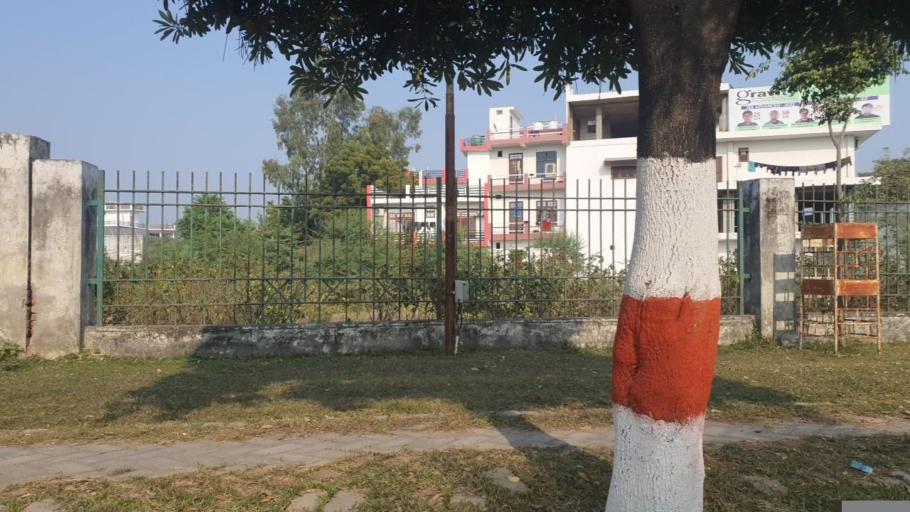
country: IN
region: Uttar Pradesh
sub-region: Lucknow District
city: Lucknow
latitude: 26.7948
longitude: 81.0090
